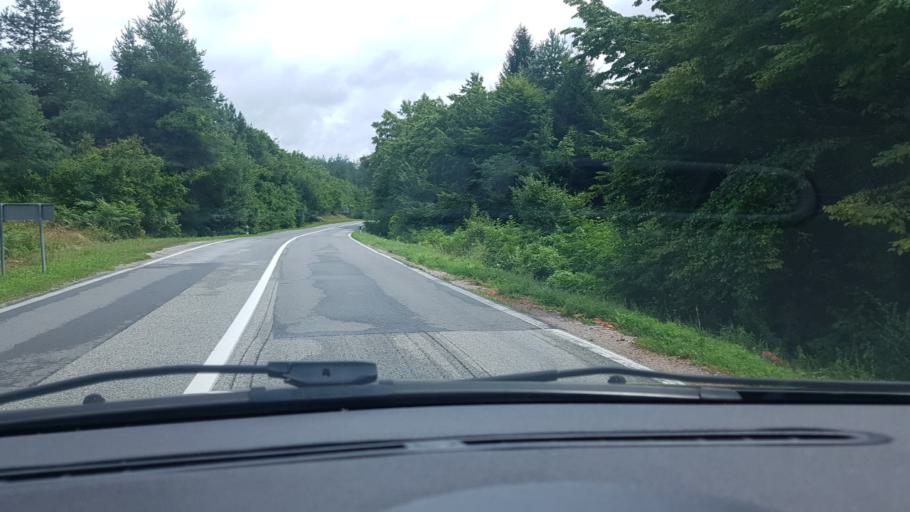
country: HR
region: Licko-Senjska
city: Jezerce
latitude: 44.9392
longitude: 15.6808
